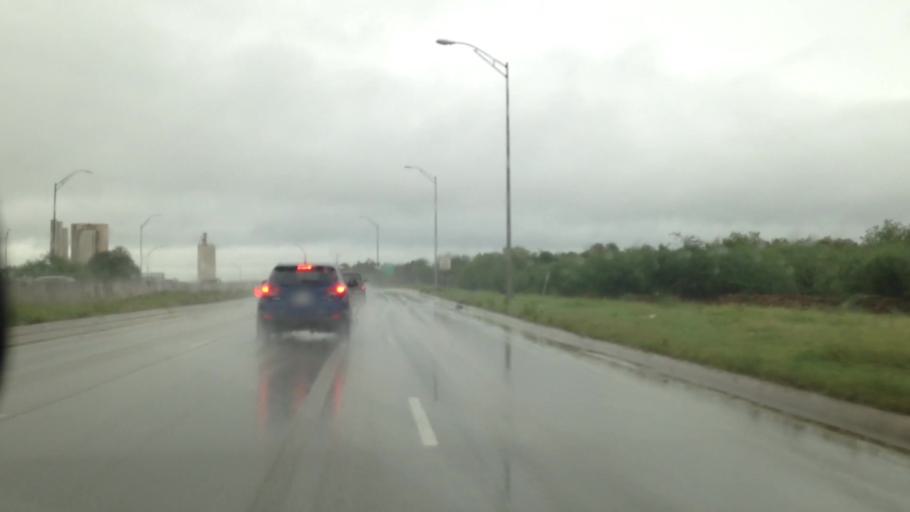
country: US
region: Texas
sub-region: Bexar County
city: Windcrest
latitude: 29.5353
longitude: -98.4052
